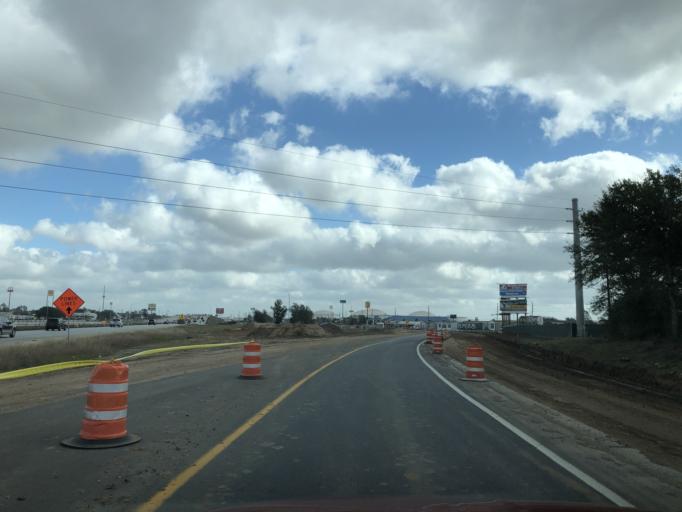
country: US
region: Texas
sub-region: Austin County
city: Sealy
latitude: 29.7621
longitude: -96.1598
